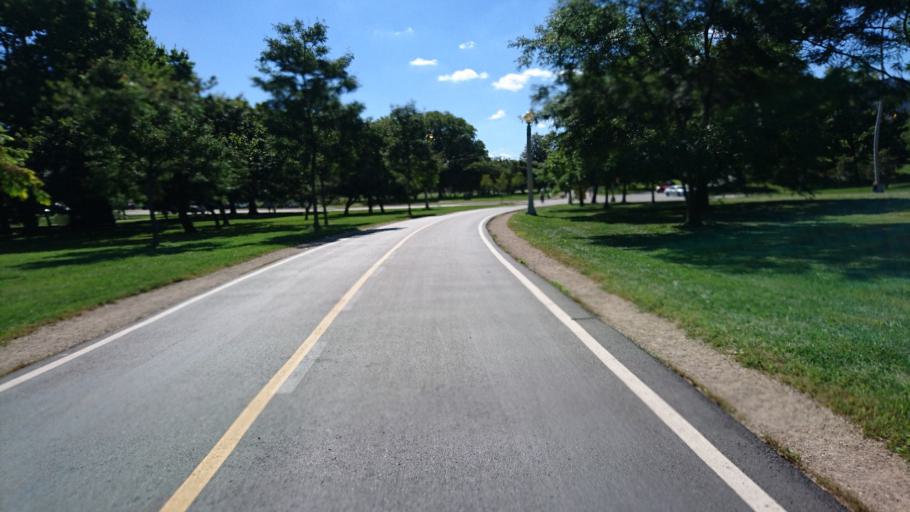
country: US
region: Illinois
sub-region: Cook County
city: Evanston
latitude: 41.9666
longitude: -87.6465
